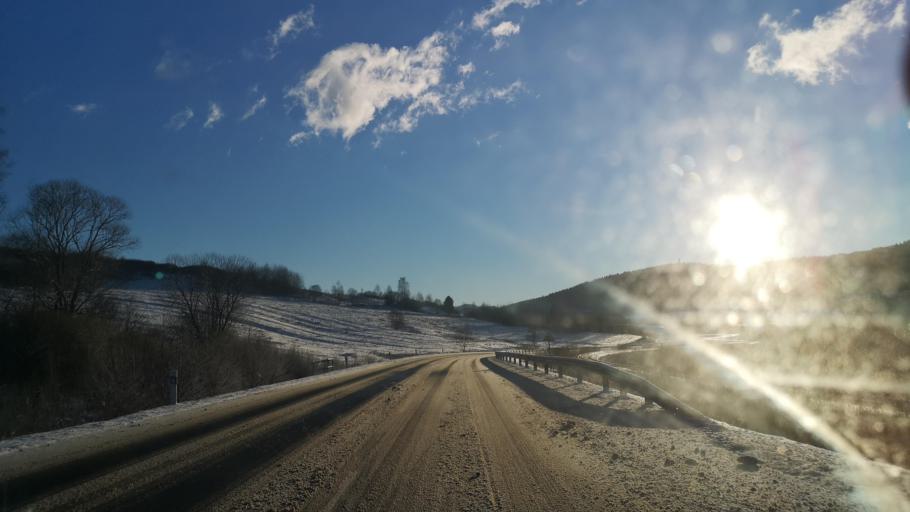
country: SK
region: Zilinsky
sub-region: Okres Liptovsky Mikulas
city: Hybe
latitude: 48.8521
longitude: 19.8320
